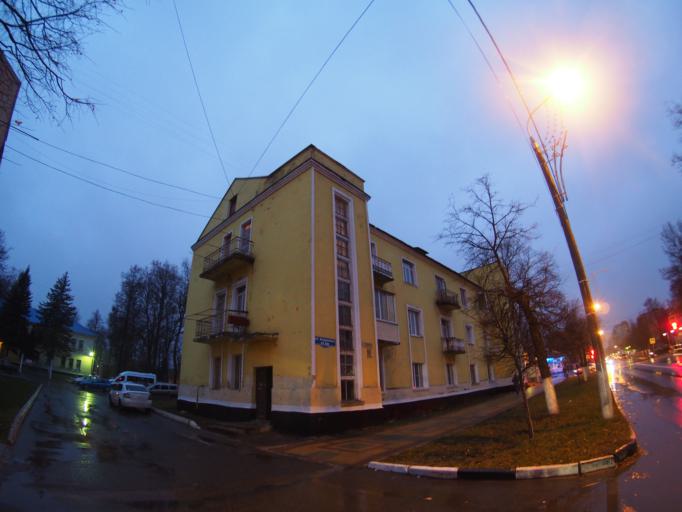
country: RU
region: Moskovskaya
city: Stupino
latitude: 54.8872
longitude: 38.0731
